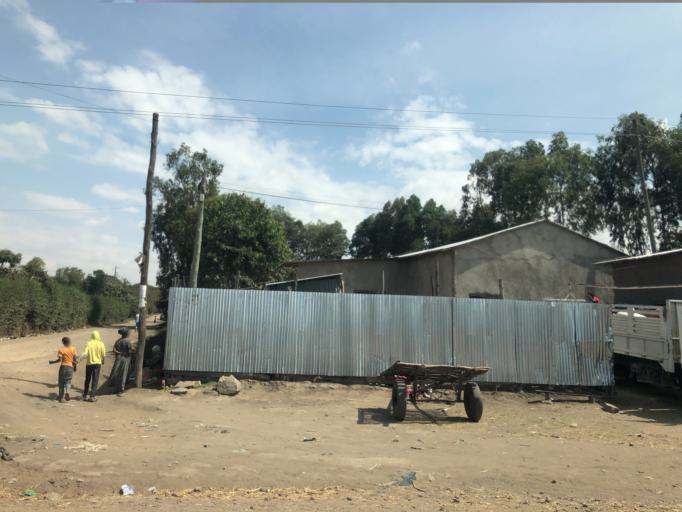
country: ET
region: Oromiya
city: Shashemene
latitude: 7.3417
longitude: 38.6700
